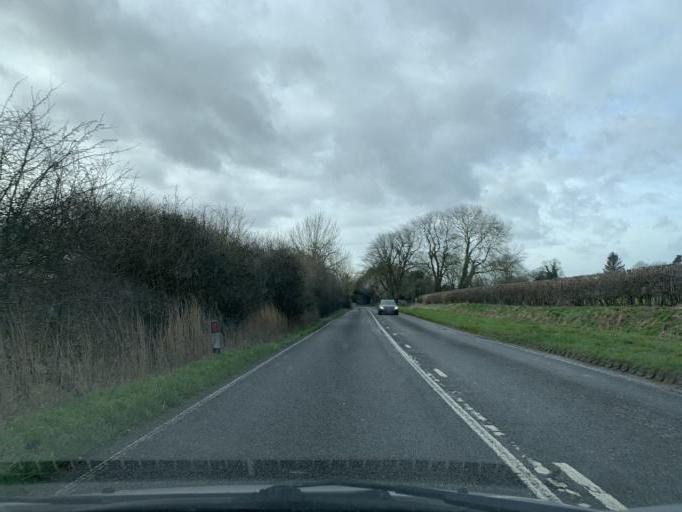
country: GB
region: England
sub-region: Hampshire
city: Fordingbridge
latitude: 50.9636
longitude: -1.7714
